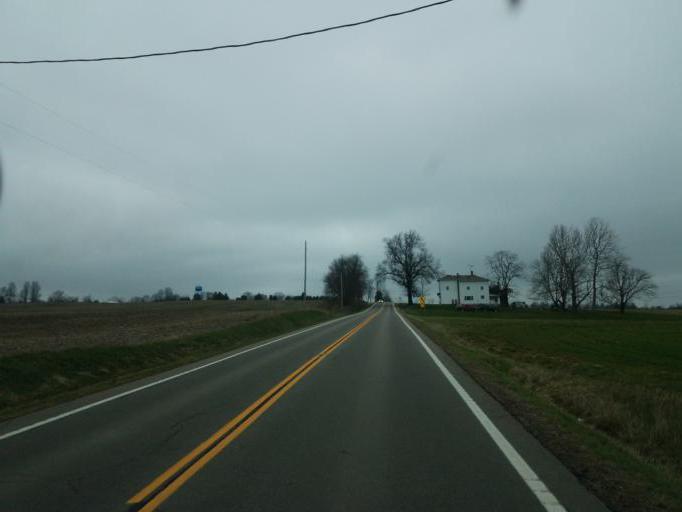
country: US
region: Ohio
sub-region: Ashland County
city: Ashland
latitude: 40.7640
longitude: -82.2597
